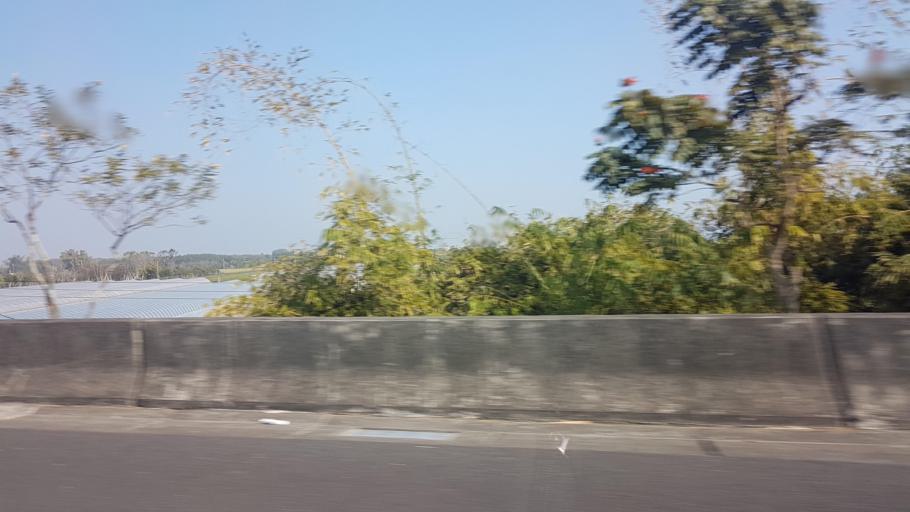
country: TW
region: Taiwan
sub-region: Chiayi
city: Taibao
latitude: 23.4219
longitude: 120.3687
